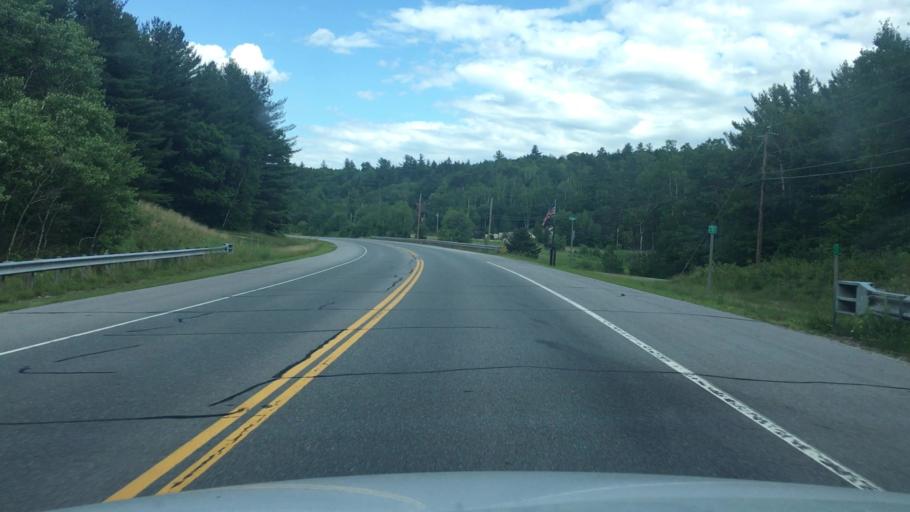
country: US
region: New Hampshire
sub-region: Coos County
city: Gorham
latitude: 44.3966
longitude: -71.0690
